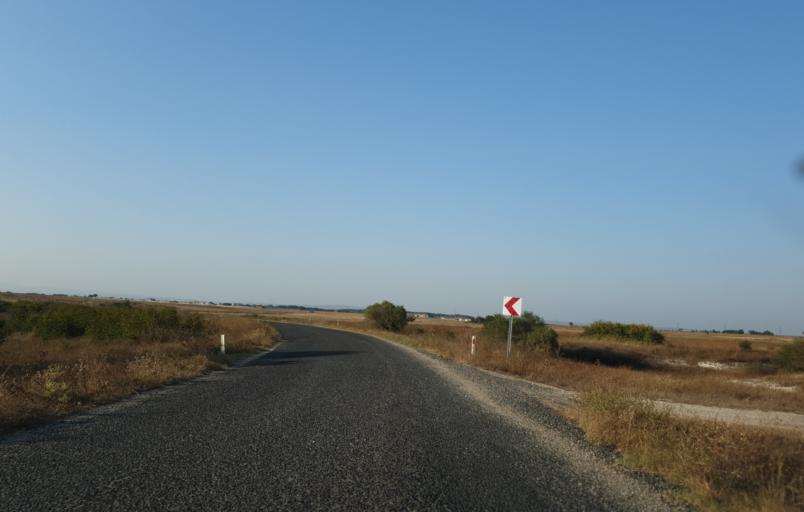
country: TR
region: Tekirdag
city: Beyazkoy
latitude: 41.4167
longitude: 27.7642
